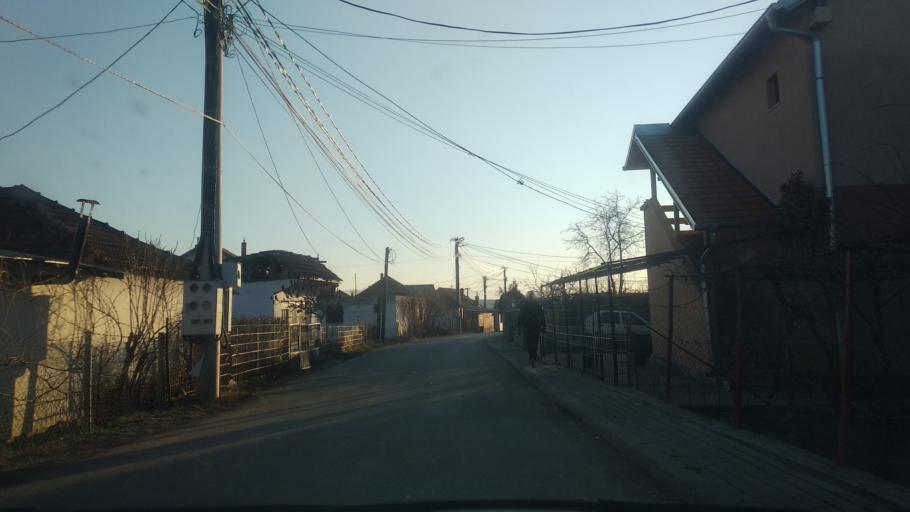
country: XK
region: Pristina
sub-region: Komuna e Prishtines
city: Pristina
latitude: 42.6060
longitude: 21.1837
